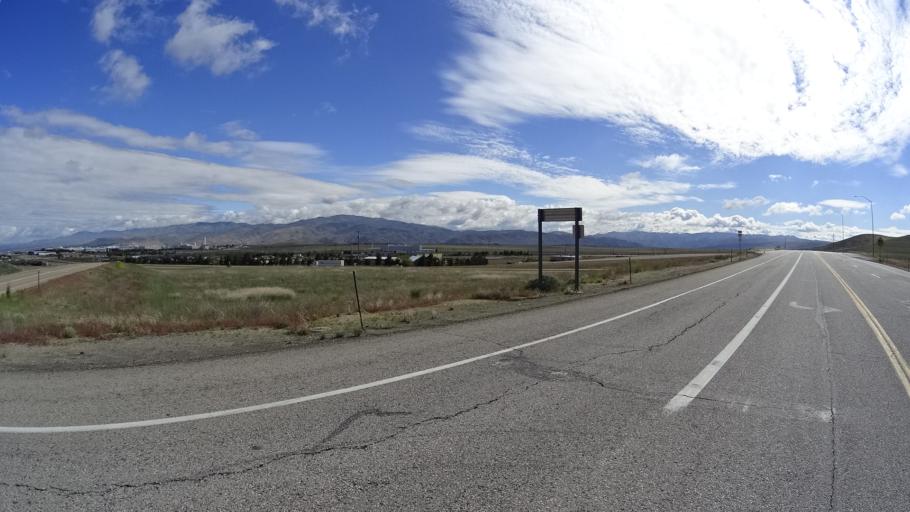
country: US
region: Idaho
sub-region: Ada County
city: Boise
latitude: 43.5076
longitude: -116.1455
